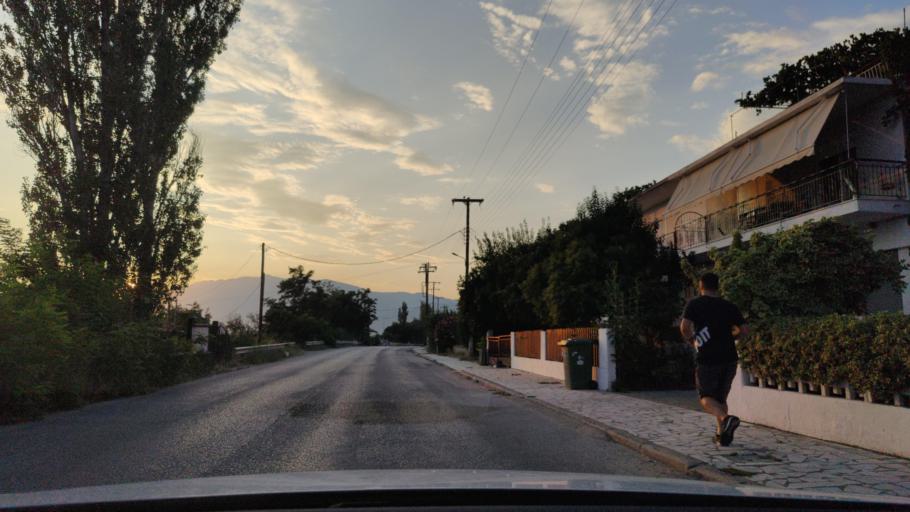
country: GR
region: Central Macedonia
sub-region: Nomos Serron
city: Sidirokastro
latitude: 41.2415
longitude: 23.3858
